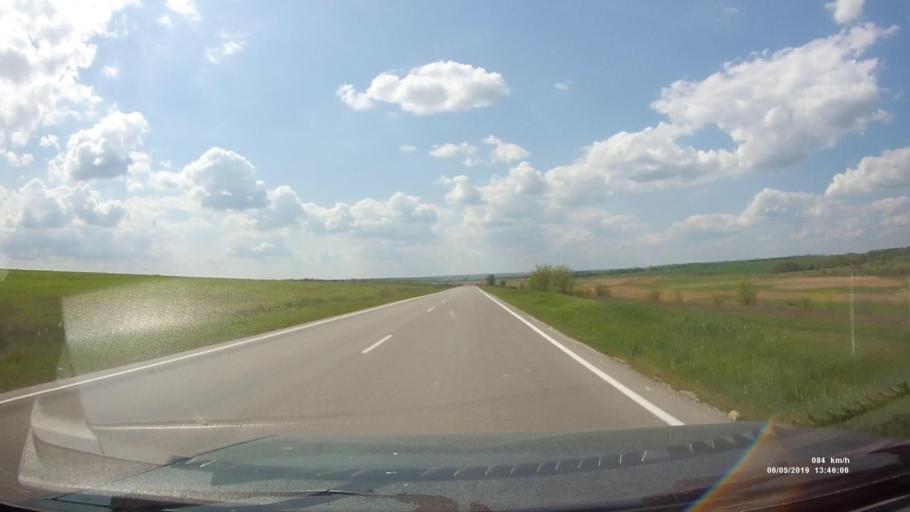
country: RU
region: Rostov
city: Melikhovskaya
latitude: 47.6577
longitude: 40.5882
